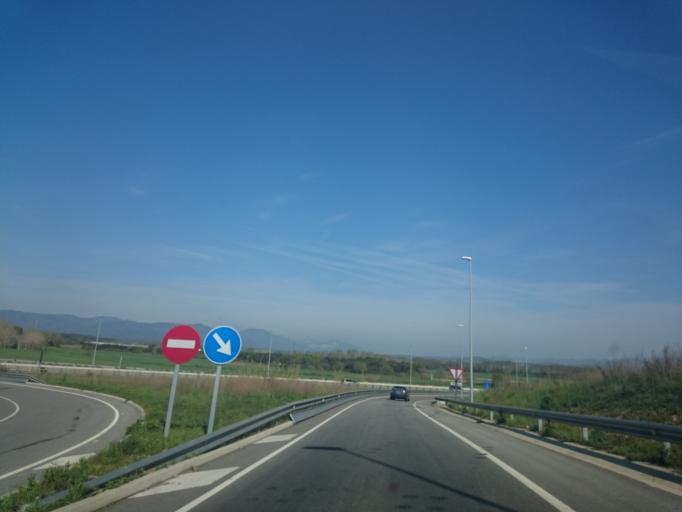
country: ES
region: Catalonia
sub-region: Provincia de Girona
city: Vilobi d'Onyar
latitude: 41.8692
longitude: 2.7789
